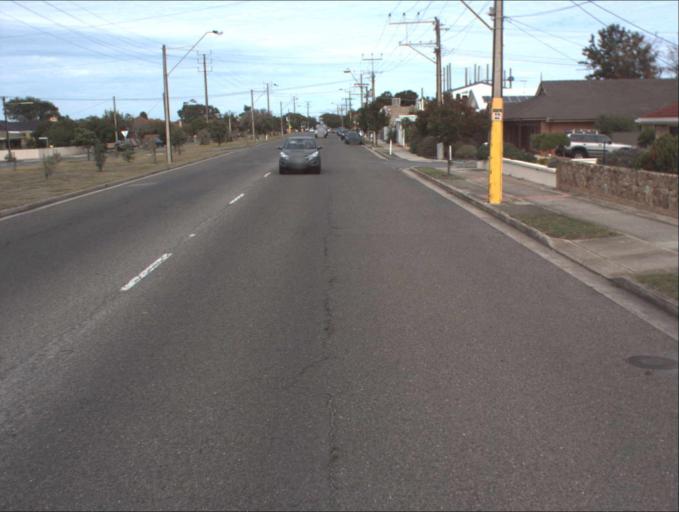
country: AU
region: South Australia
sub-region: Port Adelaide Enfield
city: Birkenhead
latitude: -34.8132
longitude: 138.4943
